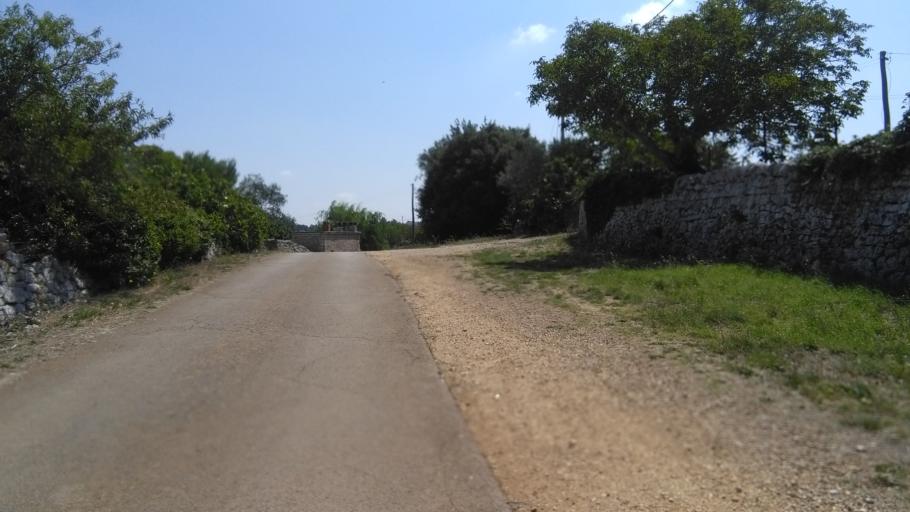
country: IT
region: Apulia
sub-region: Provincia di Bari
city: Putignano
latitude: 40.8267
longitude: 17.1381
